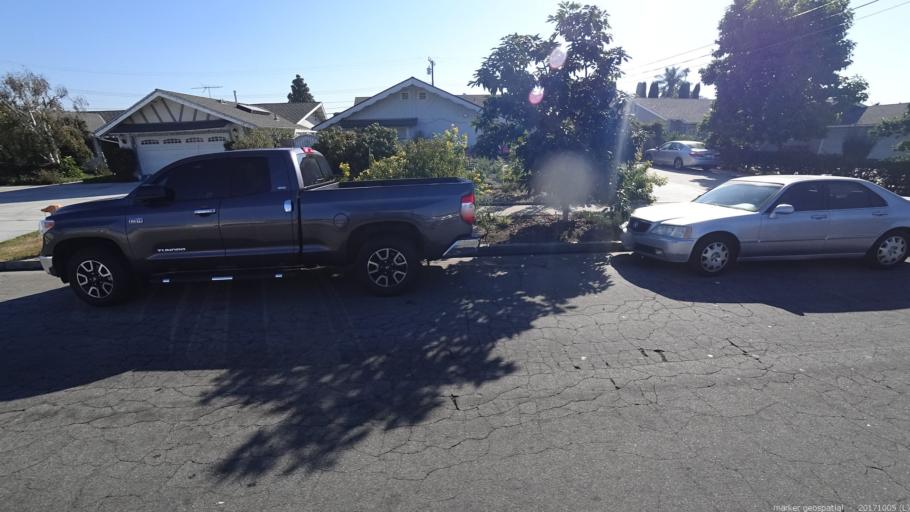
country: US
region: California
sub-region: Orange County
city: Stanton
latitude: 33.8008
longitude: -117.9637
